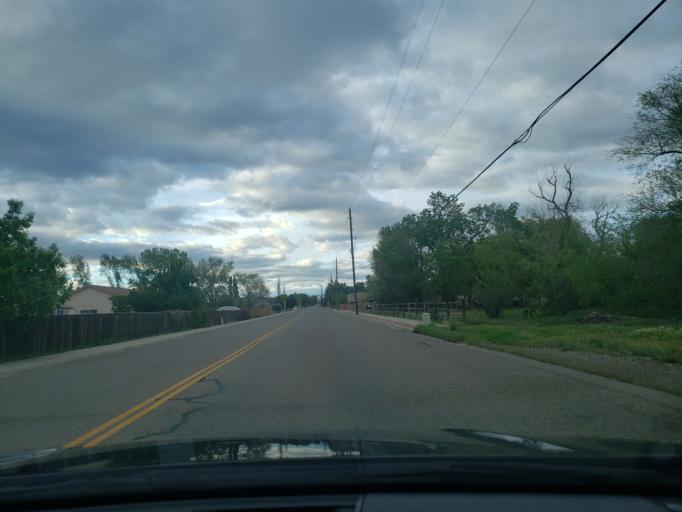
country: US
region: Colorado
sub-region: Mesa County
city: Fruita
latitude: 39.1704
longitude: -108.7290
